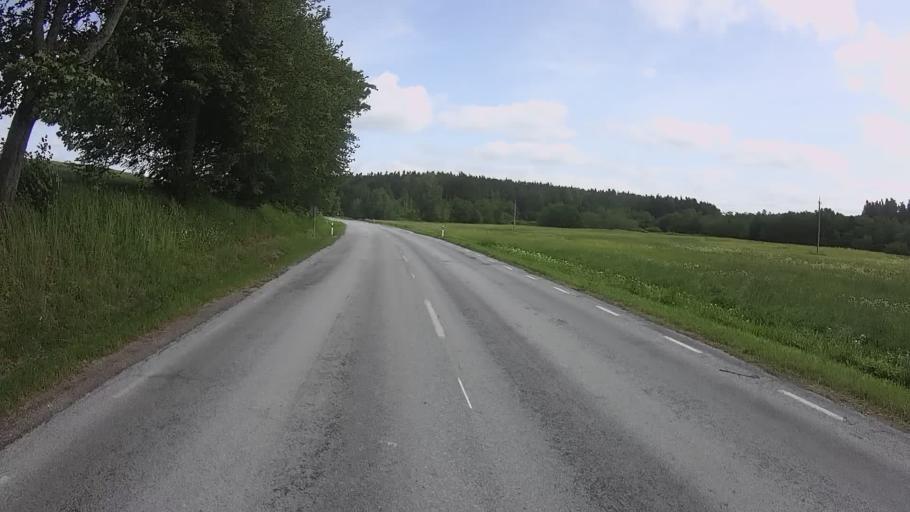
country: EE
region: Vorumaa
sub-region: Voru linn
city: Voru
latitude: 57.8564
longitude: 26.8274
